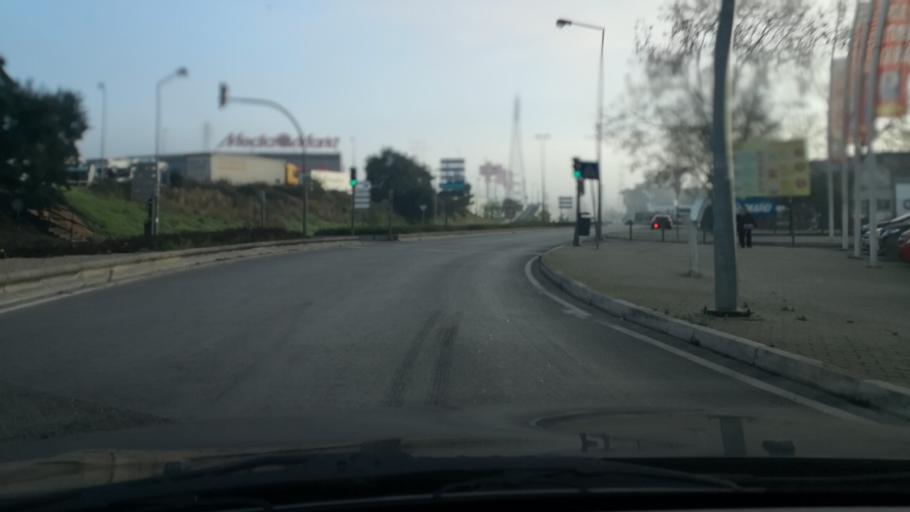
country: PT
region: Setubal
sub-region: Setubal
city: Setubal
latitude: 38.5347
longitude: -8.8667
